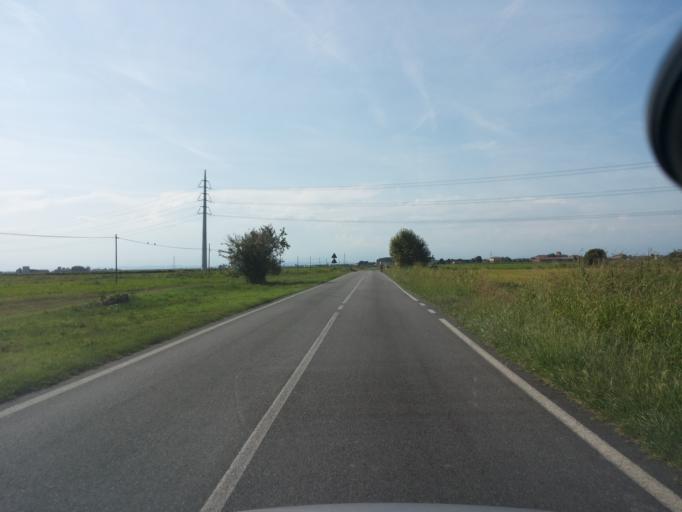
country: IT
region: Piedmont
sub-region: Provincia di Vercelli
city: Desana
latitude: 45.2756
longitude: 8.3530
